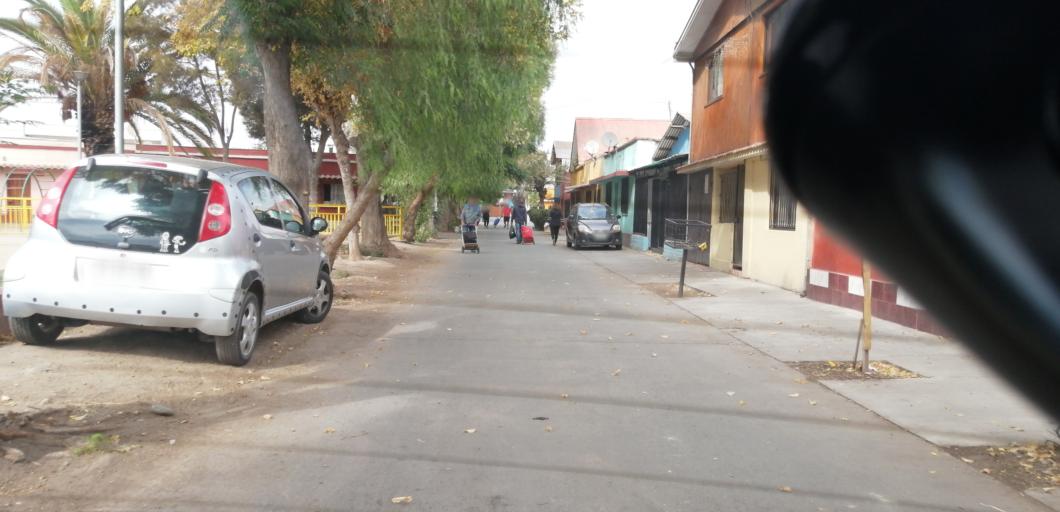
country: CL
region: Santiago Metropolitan
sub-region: Provincia de Santiago
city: Lo Prado
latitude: -33.4341
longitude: -70.7490
